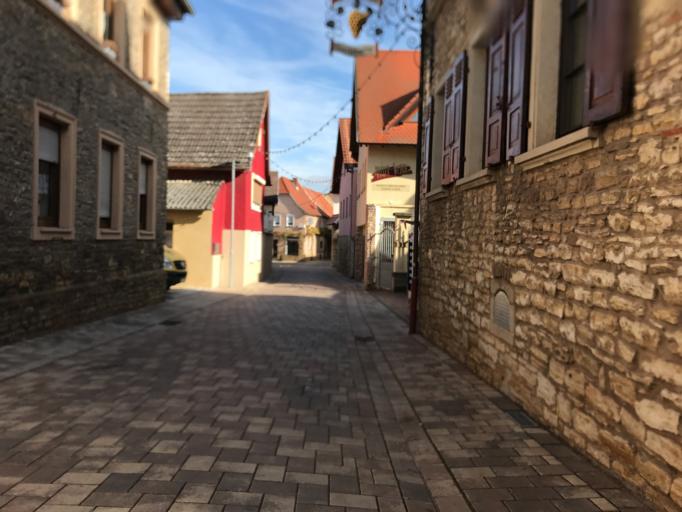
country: DE
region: Rheinland-Pfalz
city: Gau-Algesheim
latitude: 49.9571
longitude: 8.0160
